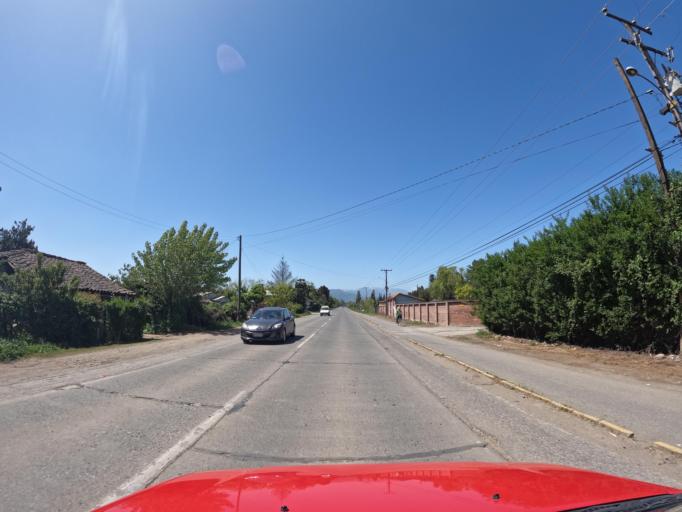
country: CL
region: Maule
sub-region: Provincia de Linares
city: Linares
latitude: -35.8299
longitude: -71.5099
